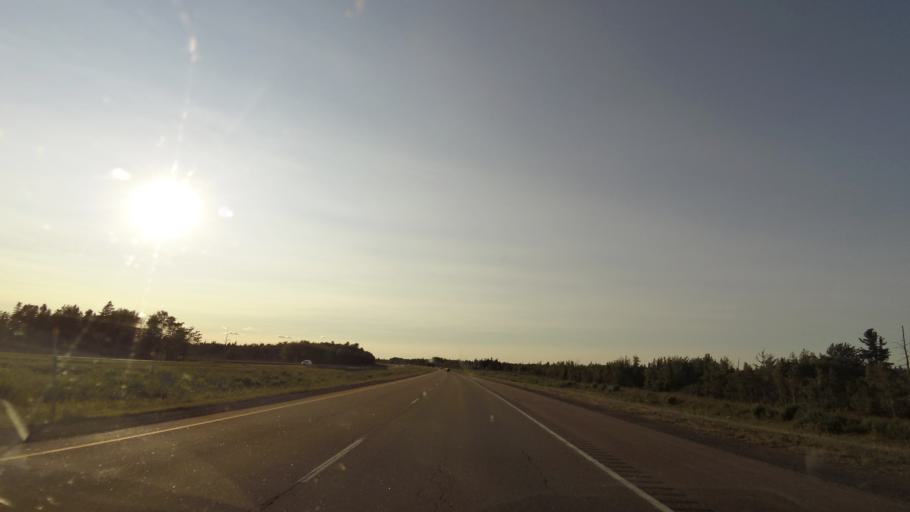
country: CA
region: New Brunswick
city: Dieppe
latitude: 46.1256
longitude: -64.6386
